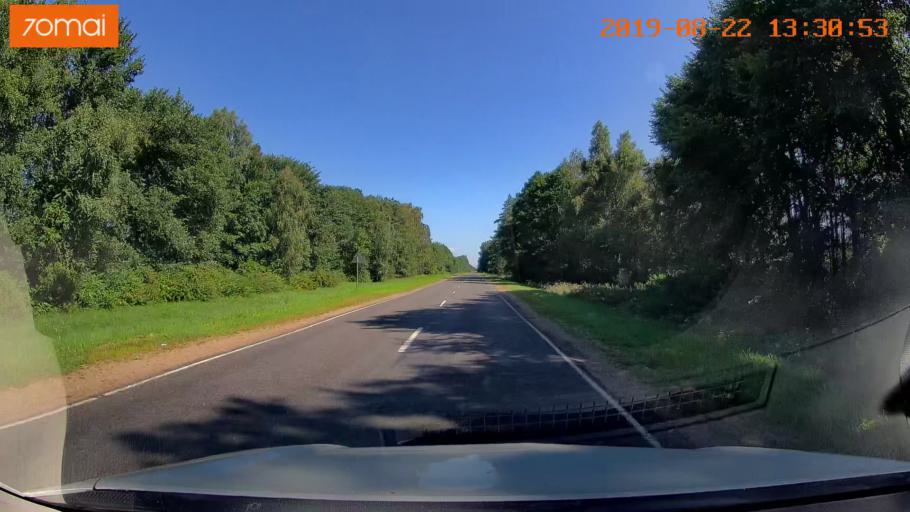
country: BY
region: Minsk
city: Staryya Darohi
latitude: 53.2173
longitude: 28.1656
